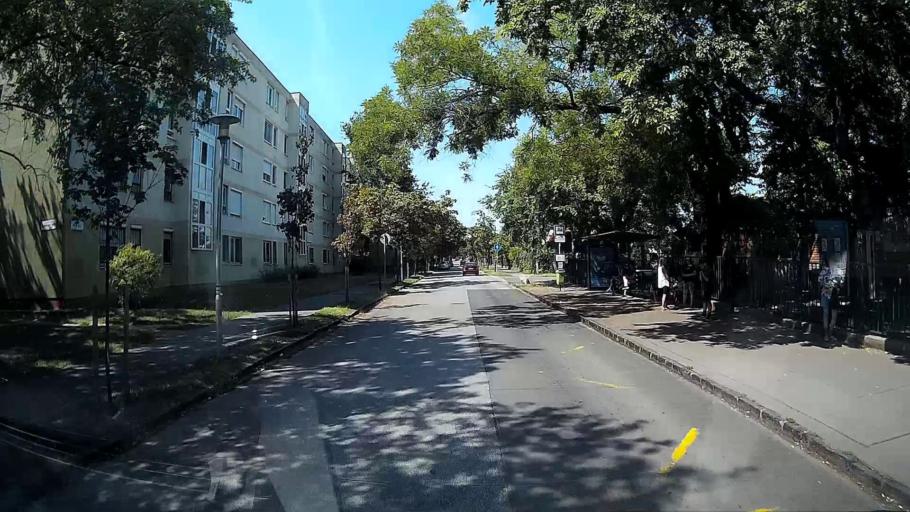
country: HU
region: Budapest
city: Budapest X. keruelet
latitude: 47.4817
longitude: 19.1516
